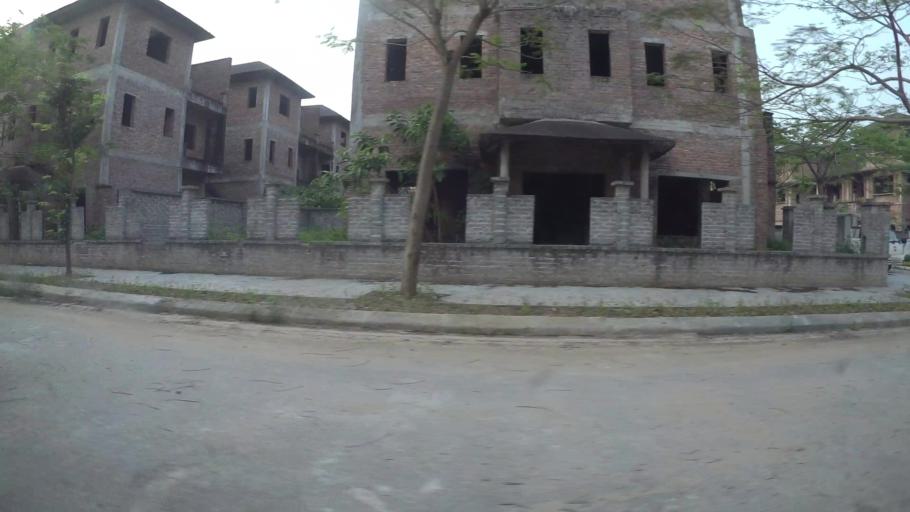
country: VN
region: Ha Noi
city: Cau Dien
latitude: 21.0001
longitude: 105.7279
